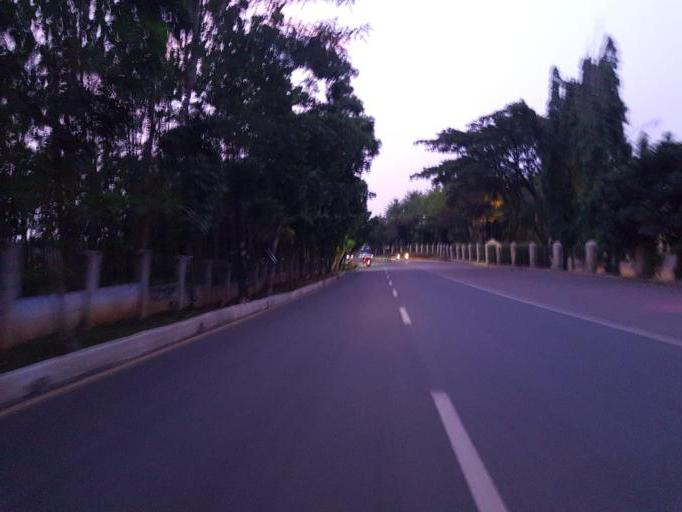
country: ID
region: West Java
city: Serpong
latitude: -6.3303
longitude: 106.6737
